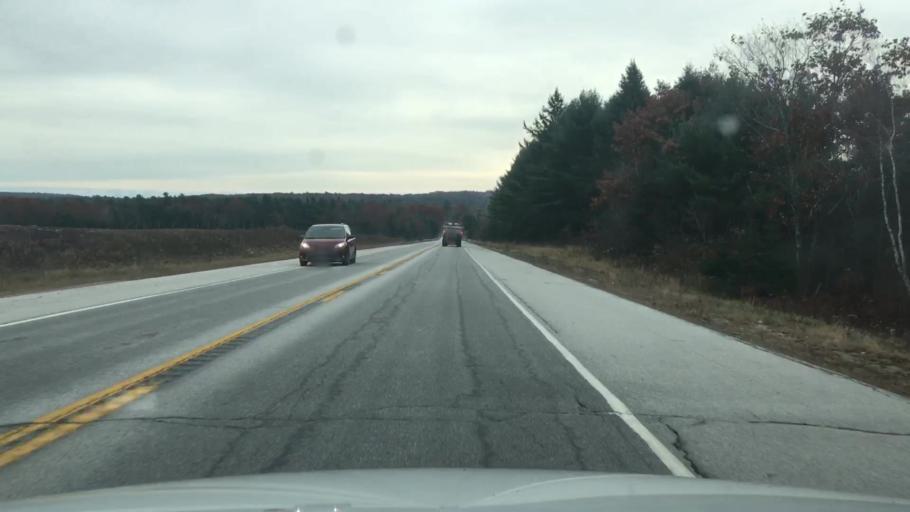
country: US
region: Maine
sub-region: Hancock County
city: Orland
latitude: 44.5715
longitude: -68.7273
